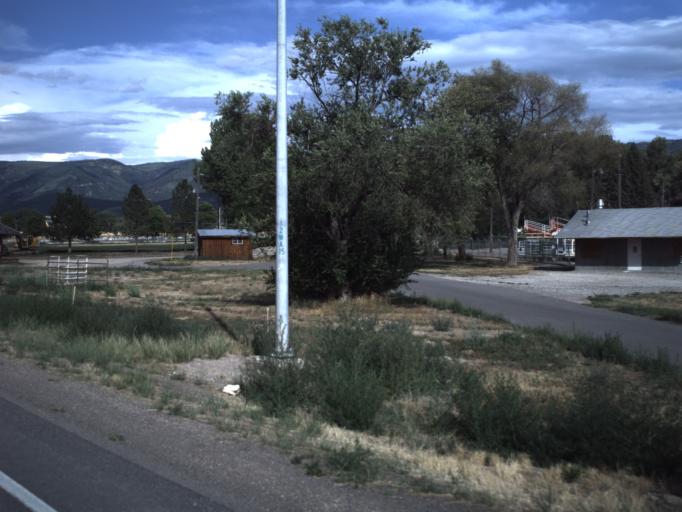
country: US
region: Utah
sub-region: Sanpete County
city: Mount Pleasant
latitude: 39.5338
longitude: -111.4584
